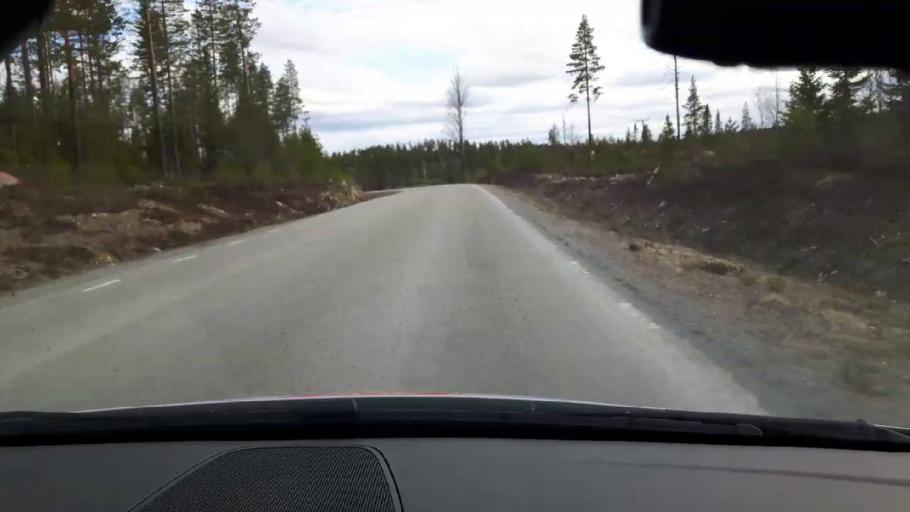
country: SE
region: Jaemtland
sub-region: Bergs Kommun
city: Hoverberg
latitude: 62.6917
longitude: 14.6312
